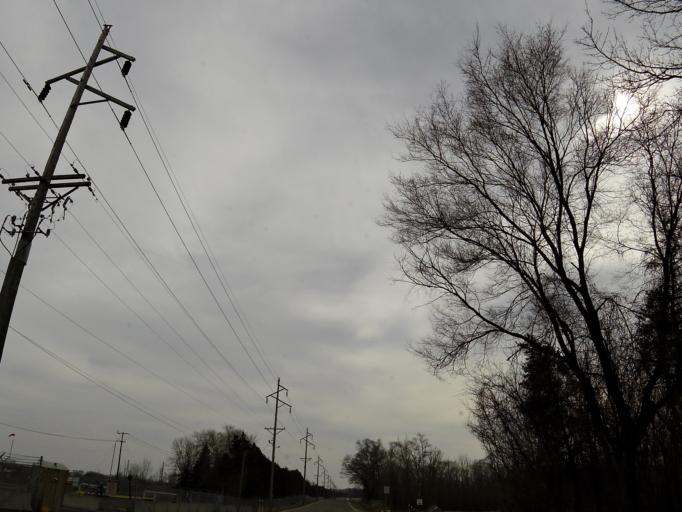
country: US
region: Minnesota
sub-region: Dakota County
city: Rosemount
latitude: 44.7685
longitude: -93.0577
